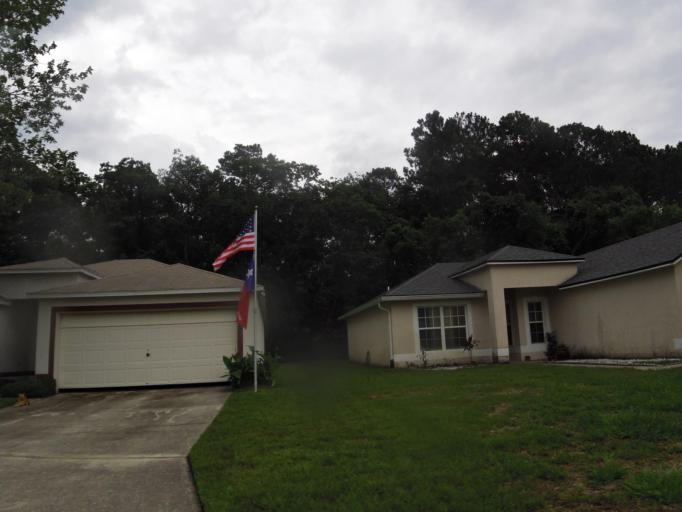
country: US
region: Florida
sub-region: Duval County
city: Jacksonville
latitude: 30.2981
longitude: -81.5423
